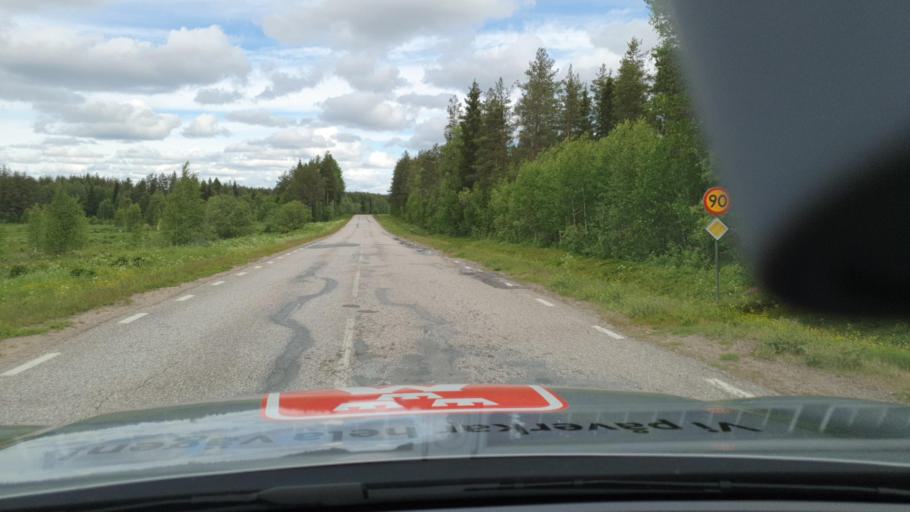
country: SE
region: Norrbotten
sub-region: Kalix Kommun
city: Kalix
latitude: 65.9789
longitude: 23.1402
